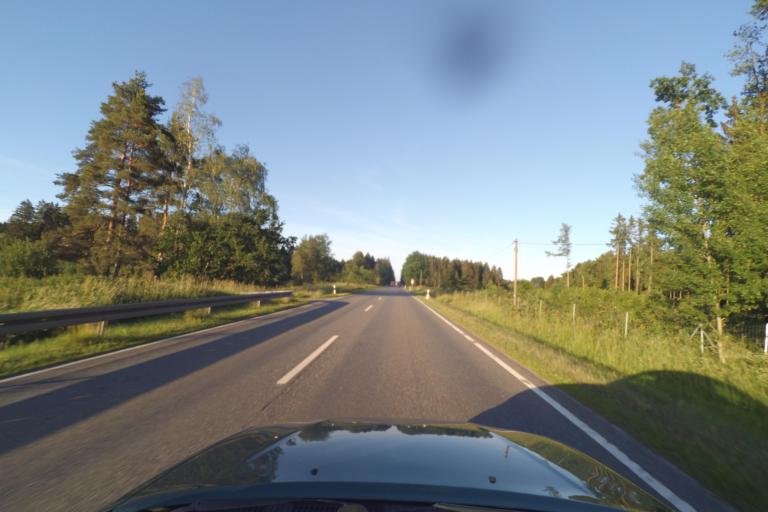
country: DE
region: Bavaria
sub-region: Upper Palatinate
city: Windischeschenbach
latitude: 49.8070
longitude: 12.2015
